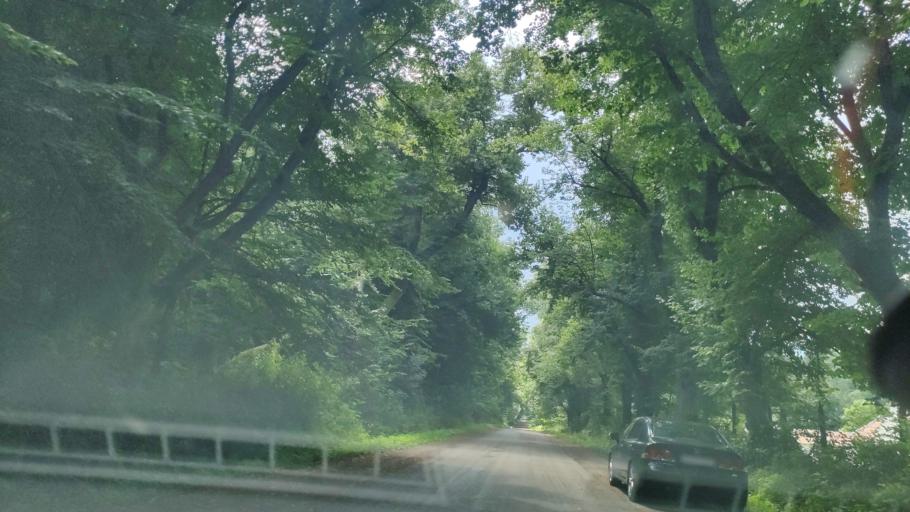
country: HU
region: Heves
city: Parad
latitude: 47.9149
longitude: 20.0586
